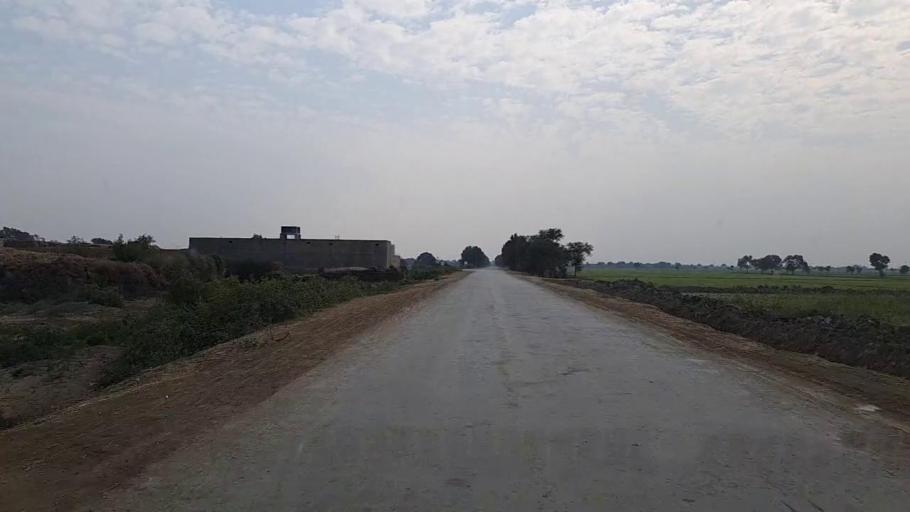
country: PK
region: Sindh
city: Mirwah Gorchani
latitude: 25.3827
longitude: 69.0818
